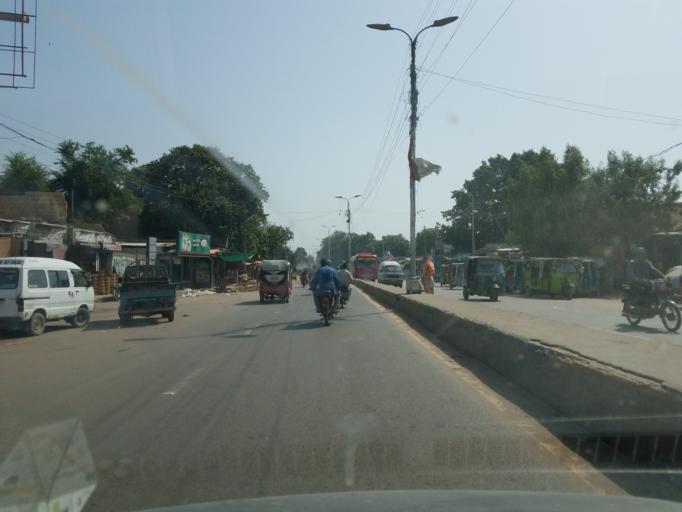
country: PK
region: Sindh
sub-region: Karachi District
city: Karachi
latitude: 24.8917
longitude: 67.0434
